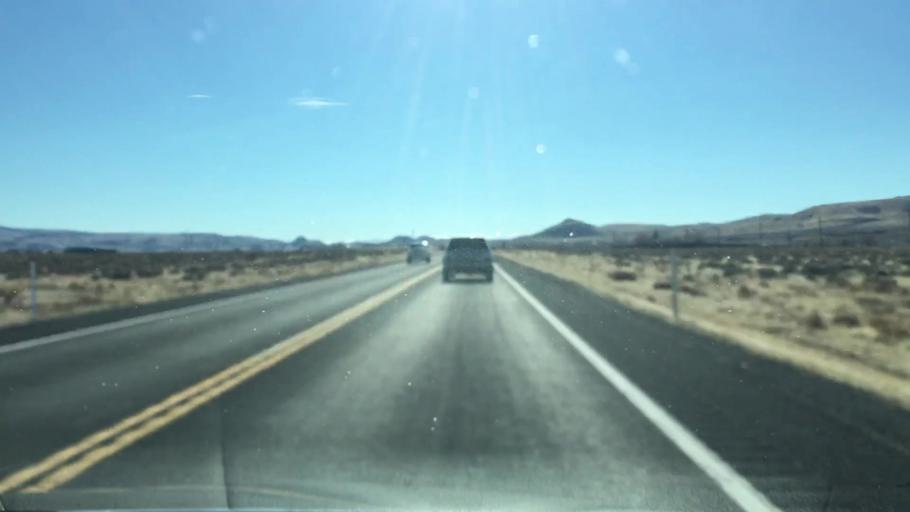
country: US
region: Nevada
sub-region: Lyon County
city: Silver Springs
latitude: 39.3721
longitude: -119.2343
